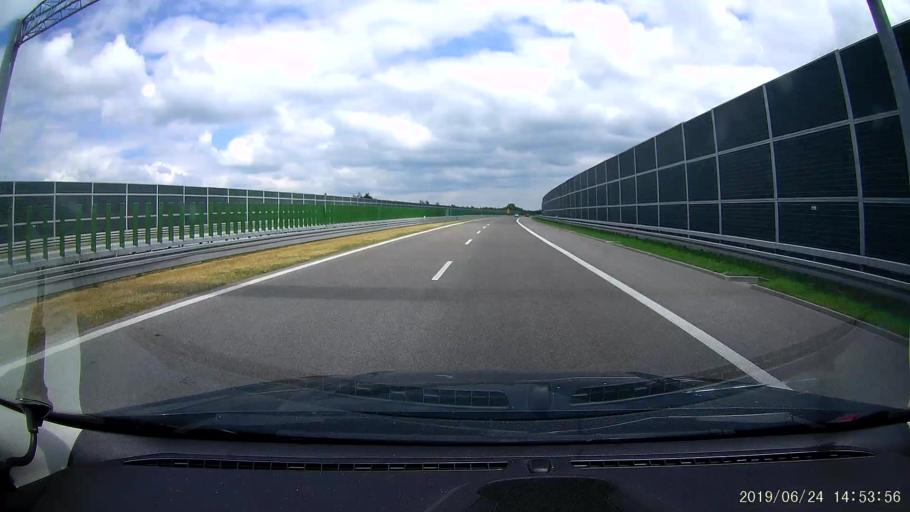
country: PL
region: Subcarpathian Voivodeship
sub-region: Powiat ropczycko-sedziszowski
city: Ostrow
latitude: 50.1088
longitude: 21.6412
